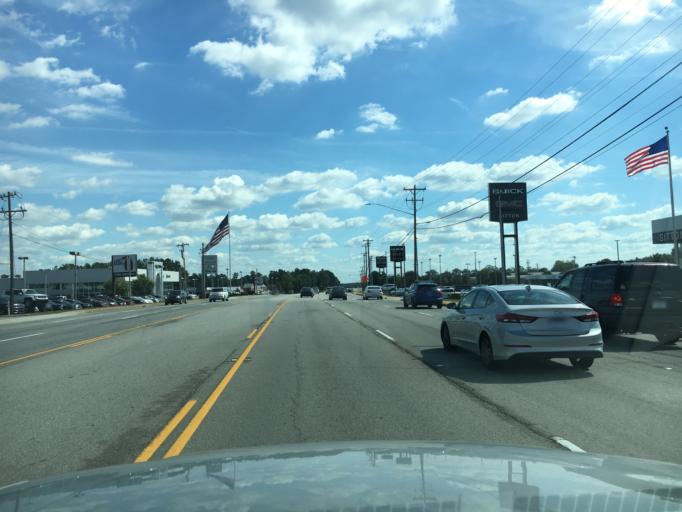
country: US
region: South Carolina
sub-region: Greenville County
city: Mauldin
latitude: 34.8237
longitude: -82.3436
